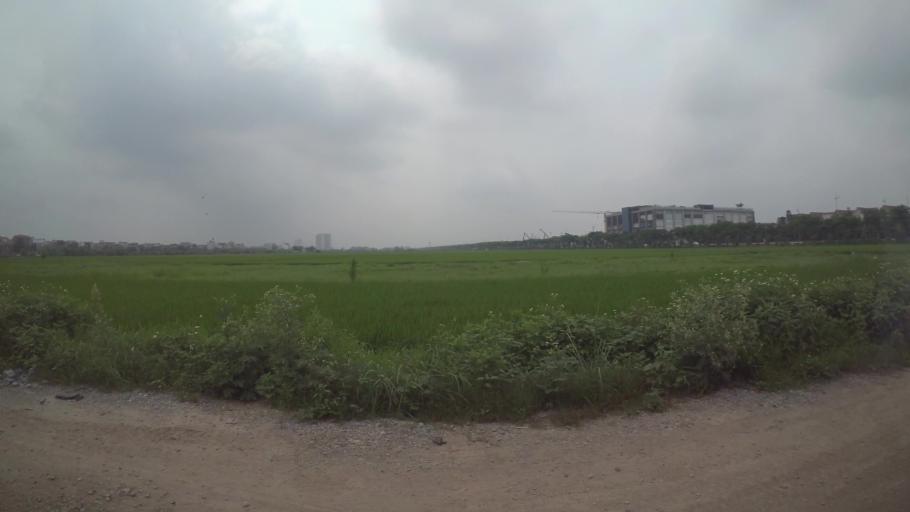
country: VN
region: Ha Noi
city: Trau Quy
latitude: 21.0542
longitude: 105.9171
